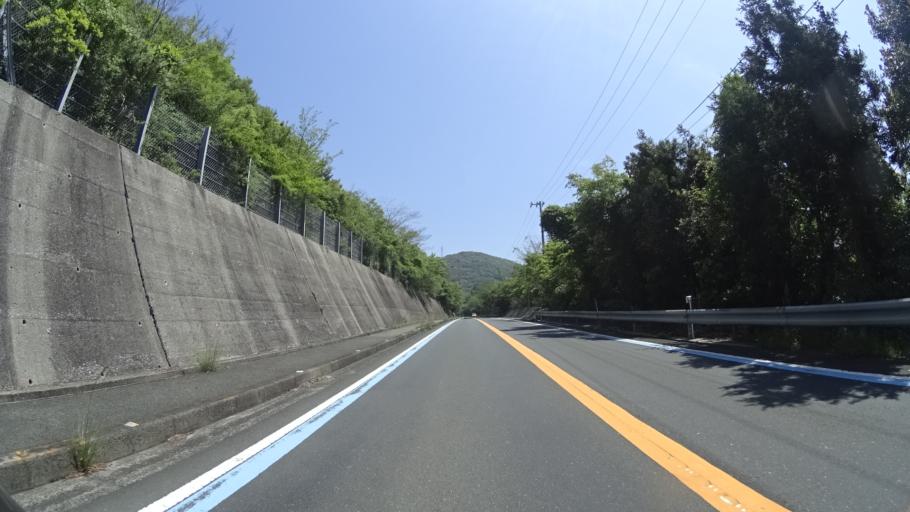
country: JP
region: Ehime
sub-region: Nishiuwa-gun
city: Ikata-cho
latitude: 33.4482
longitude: 132.2674
